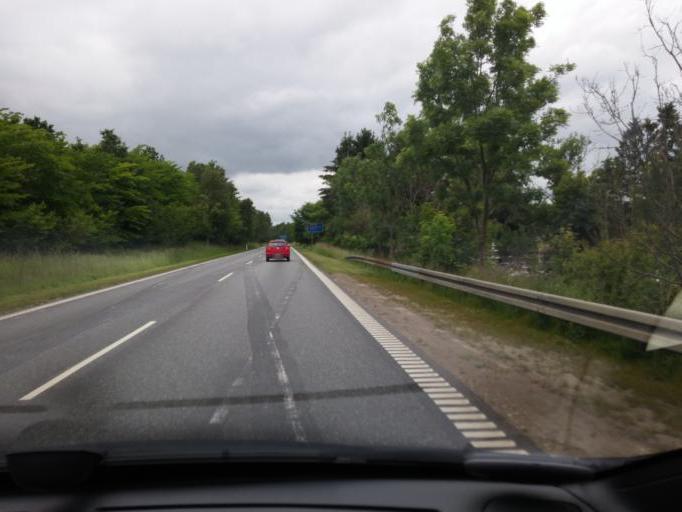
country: DK
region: Capital Region
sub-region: Hillerod Kommune
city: Nodebo
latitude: 55.9404
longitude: 12.3531
